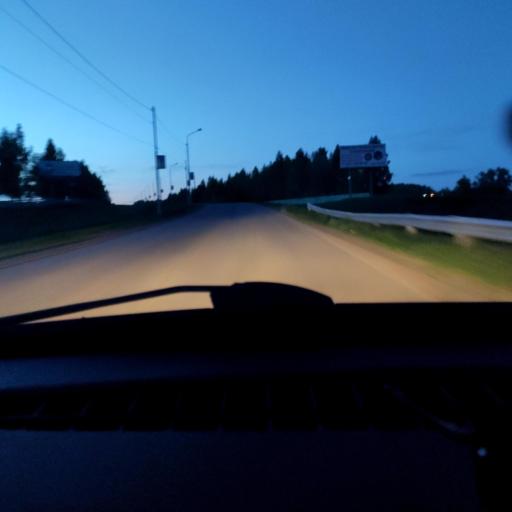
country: RU
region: Bashkortostan
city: Karmaskaly
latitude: 54.3749
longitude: 56.1751
